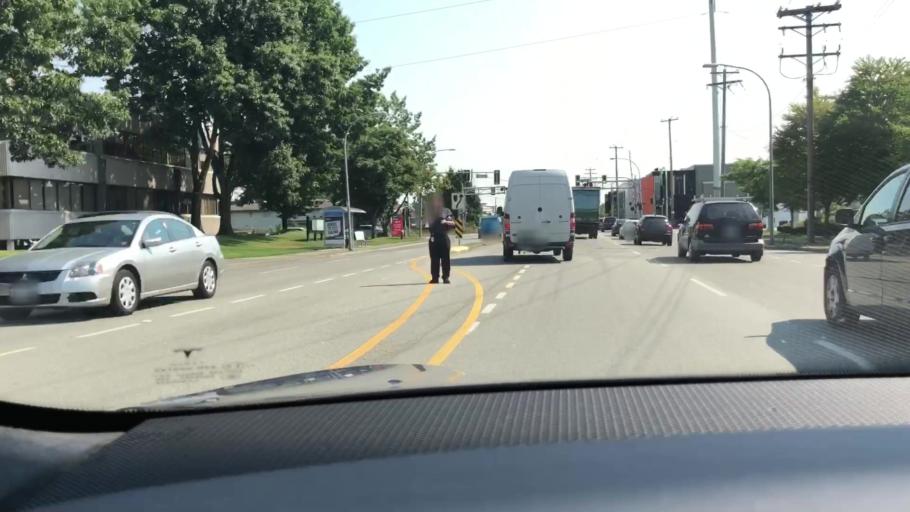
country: CA
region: British Columbia
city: Richmond
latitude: 49.1845
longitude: -123.1040
